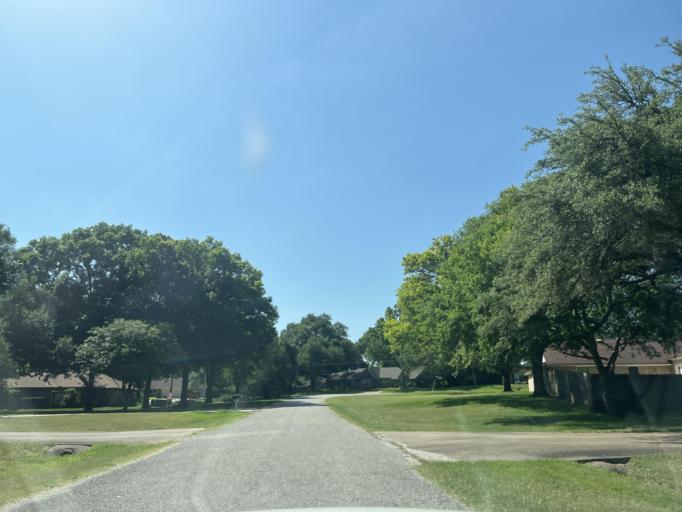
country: US
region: Texas
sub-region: Washington County
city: Brenham
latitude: 30.1512
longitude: -96.3644
